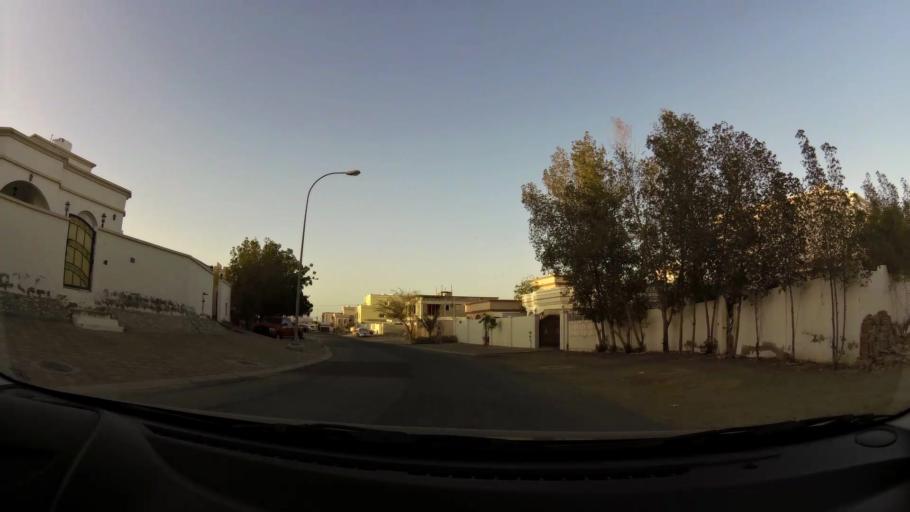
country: OM
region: Muhafazat Masqat
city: As Sib al Jadidah
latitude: 23.6009
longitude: 58.2325
